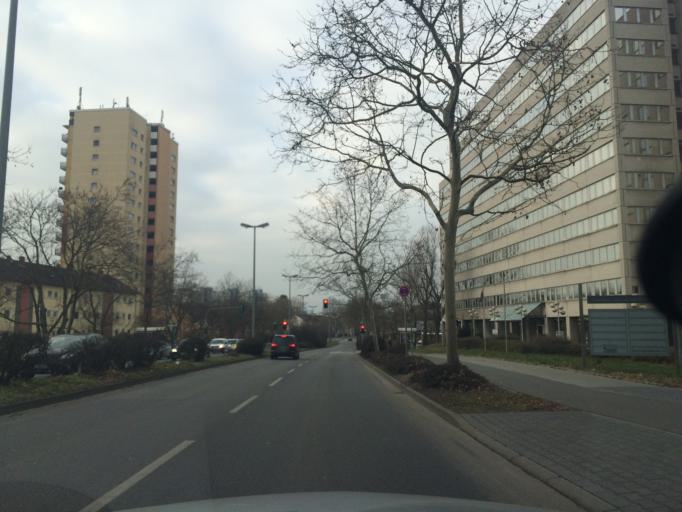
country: DE
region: Hesse
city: Niederrad
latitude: 50.1183
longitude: 8.6246
